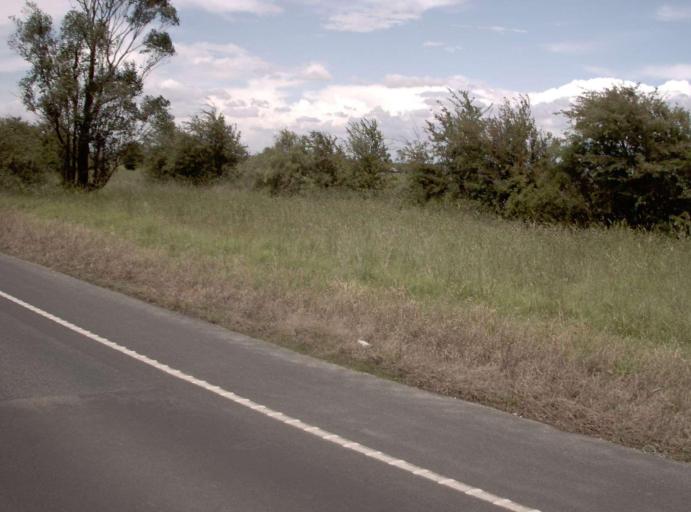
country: AU
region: Victoria
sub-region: Wellington
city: Sale
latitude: -38.0427
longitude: 147.0199
